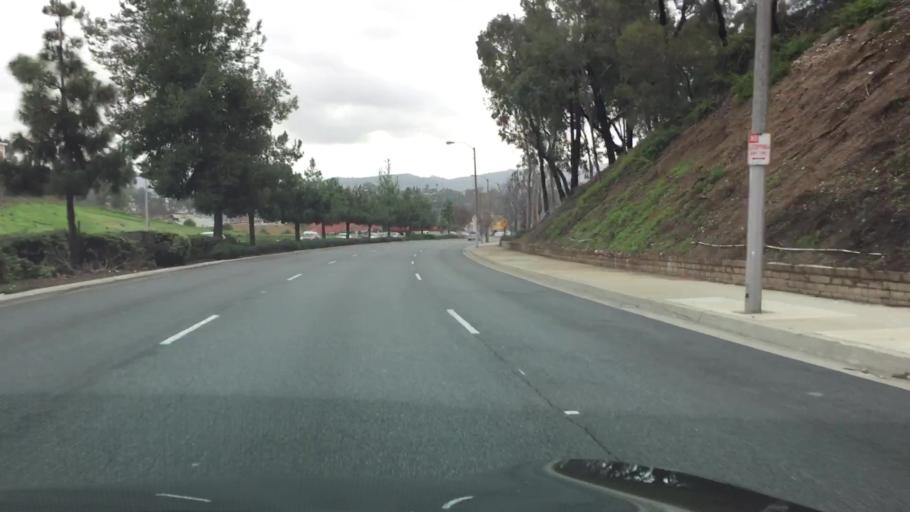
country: US
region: California
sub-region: Los Angeles County
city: South San Jose Hills
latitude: 34.0350
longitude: -117.9131
